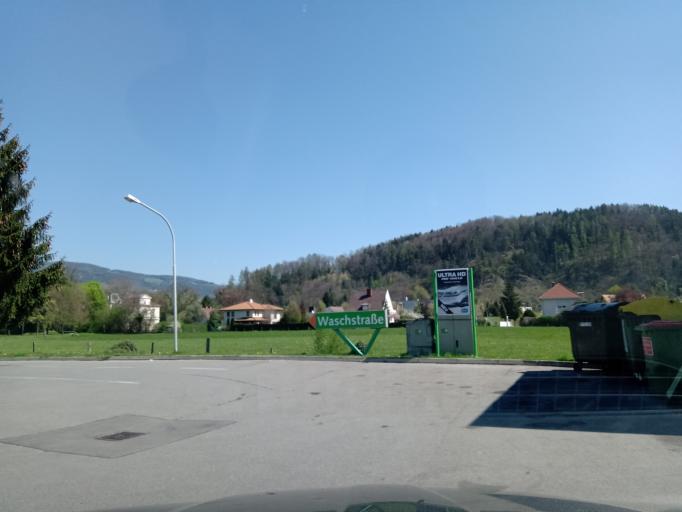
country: AT
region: Styria
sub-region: Politischer Bezirk Leoben
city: Leoben
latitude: 47.3707
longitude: 15.0923
